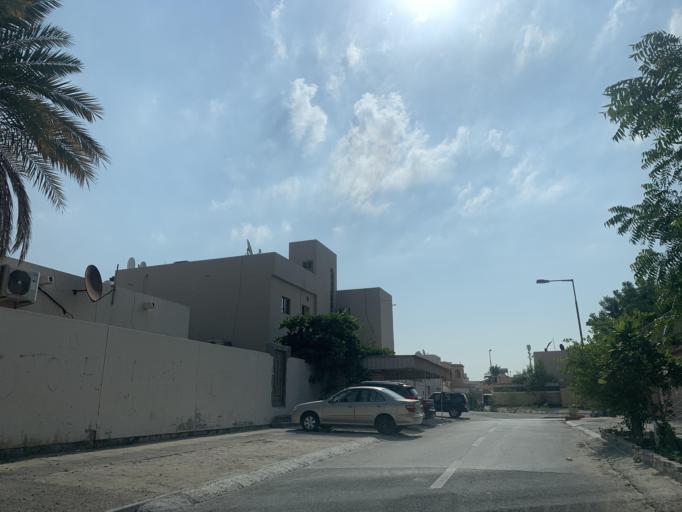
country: BH
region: Central Governorate
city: Madinat Hamad
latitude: 26.1055
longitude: 50.4998
